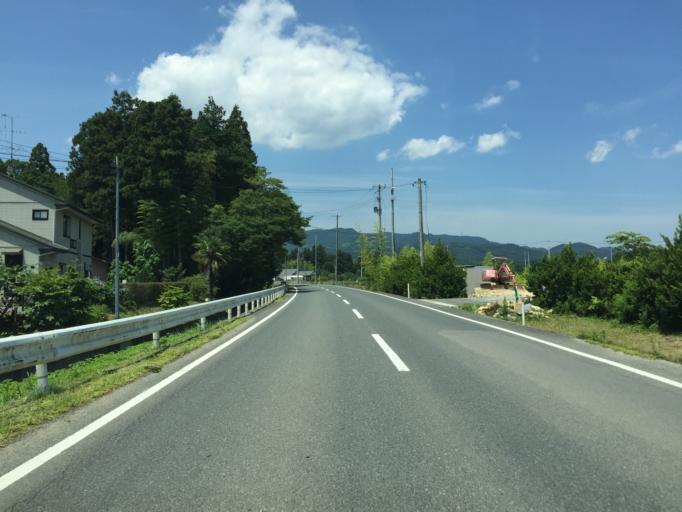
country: JP
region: Miyagi
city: Marumori
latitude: 37.7722
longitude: 140.9051
